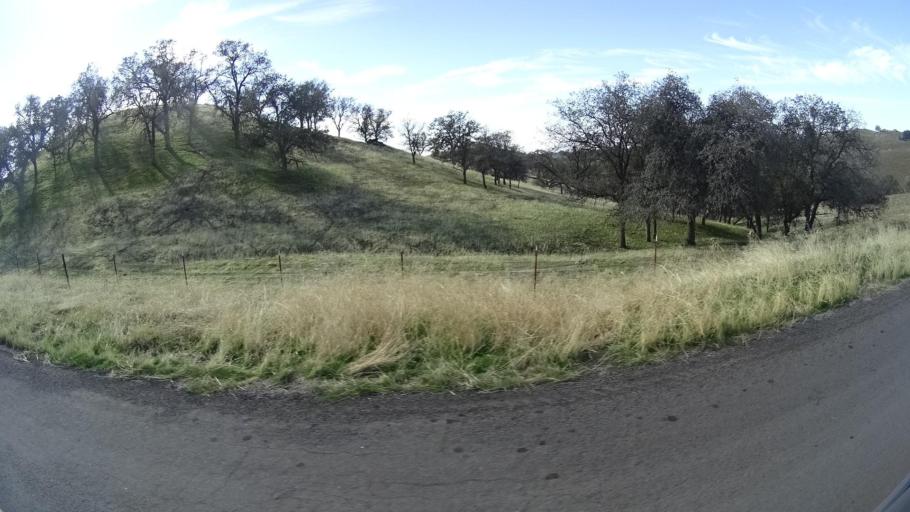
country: US
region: California
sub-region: Tulare County
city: Richgrove
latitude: 35.6612
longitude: -118.8441
